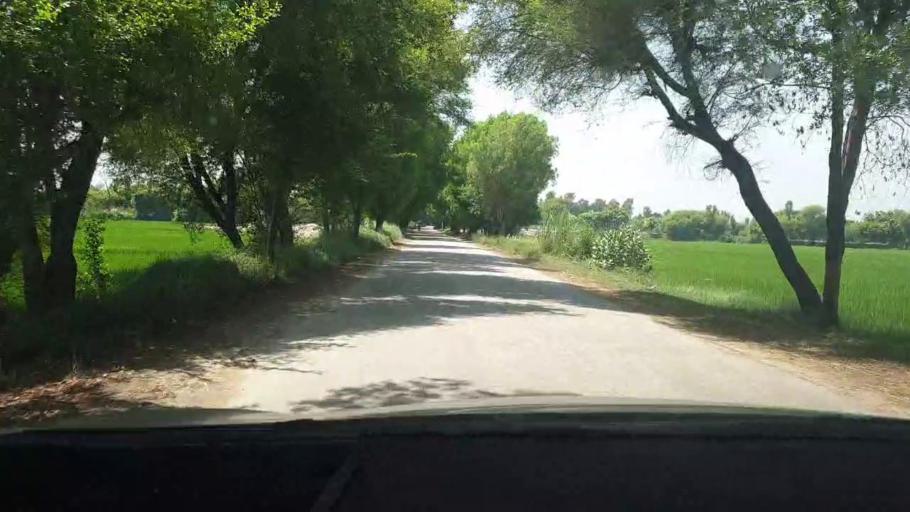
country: PK
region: Sindh
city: Miro Khan
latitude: 27.6717
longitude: 68.0520
